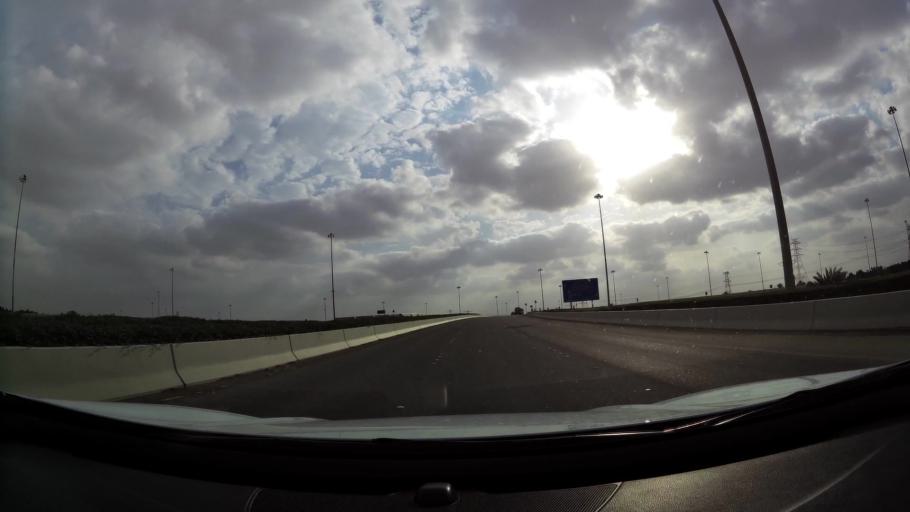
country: AE
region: Abu Dhabi
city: Abu Dhabi
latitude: 24.3295
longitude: 54.5873
